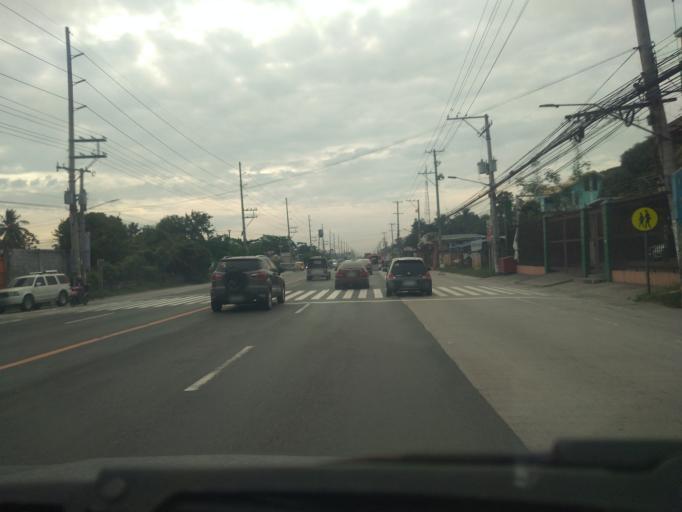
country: PH
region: Central Luzon
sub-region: Province of Pampanga
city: Bulaon
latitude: 15.0721
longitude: 120.6456
